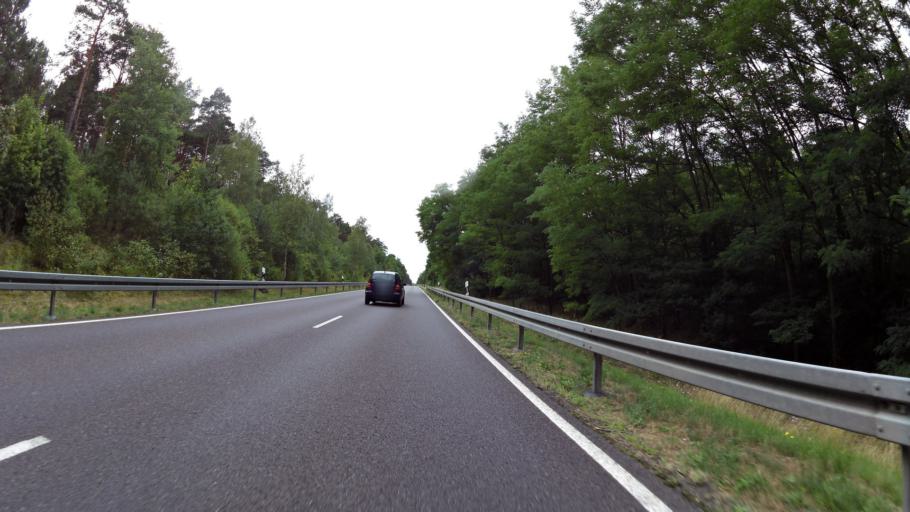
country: DE
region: Brandenburg
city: Schenkendobern
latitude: 51.8962
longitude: 14.5955
